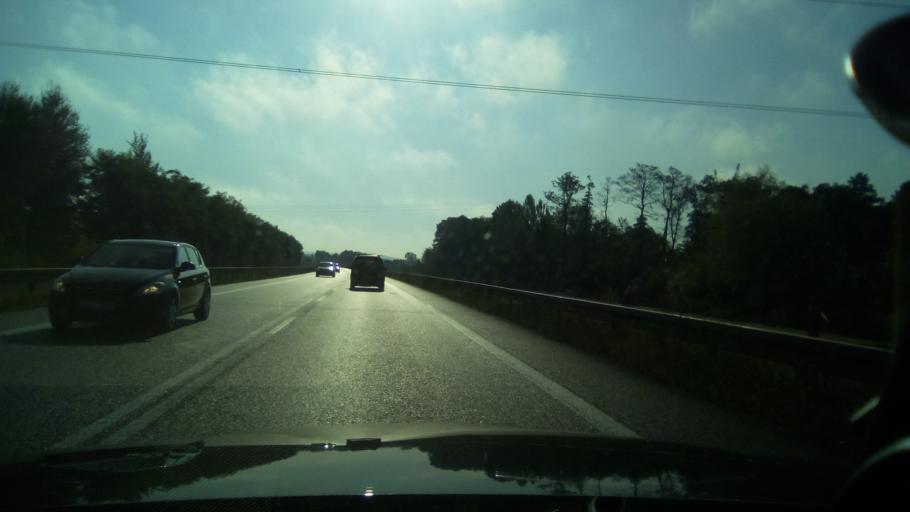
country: PL
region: Silesian Voivodeship
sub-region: Powiat bedzinski
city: Sarnow
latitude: 50.4216
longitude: 19.1883
